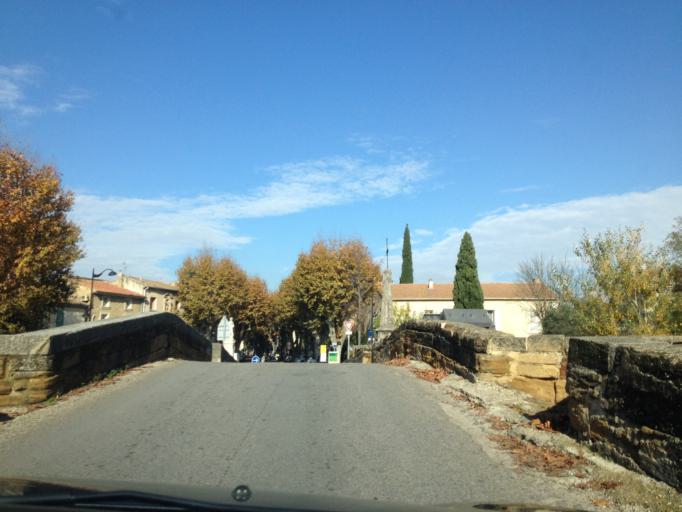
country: FR
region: Provence-Alpes-Cote d'Azur
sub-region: Departement du Vaucluse
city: Bedarrides
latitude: 44.0389
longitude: 4.9003
